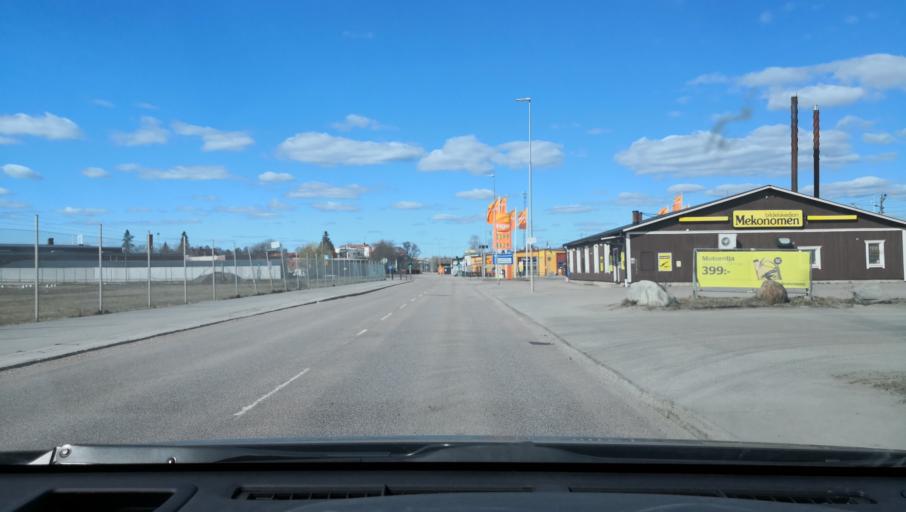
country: SE
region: Vaestmanland
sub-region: Sala Kommun
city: Sala
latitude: 59.9176
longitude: 16.6164
